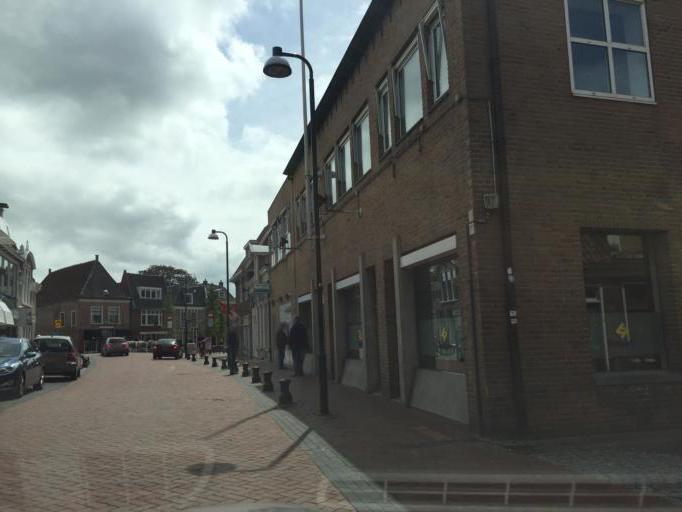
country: NL
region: Friesland
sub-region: Gemeente Dongeradeel
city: Dokkum
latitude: 53.3281
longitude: 6.0004
